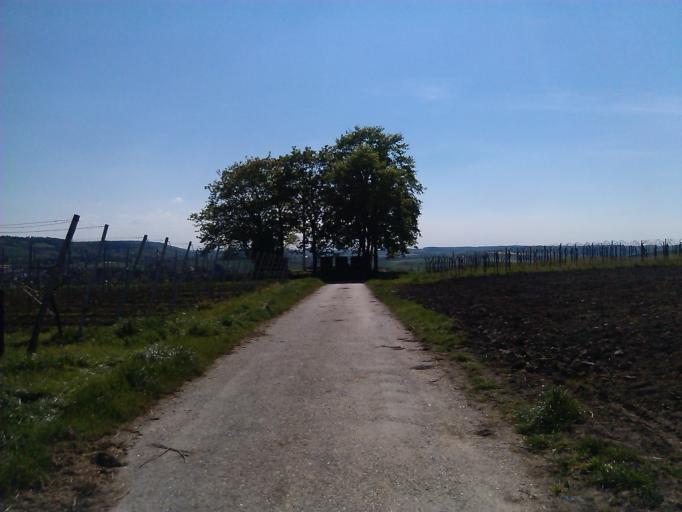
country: DE
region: Baden-Wuerttemberg
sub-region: Karlsruhe Region
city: Kurnbach
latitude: 49.0820
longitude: 8.8505
